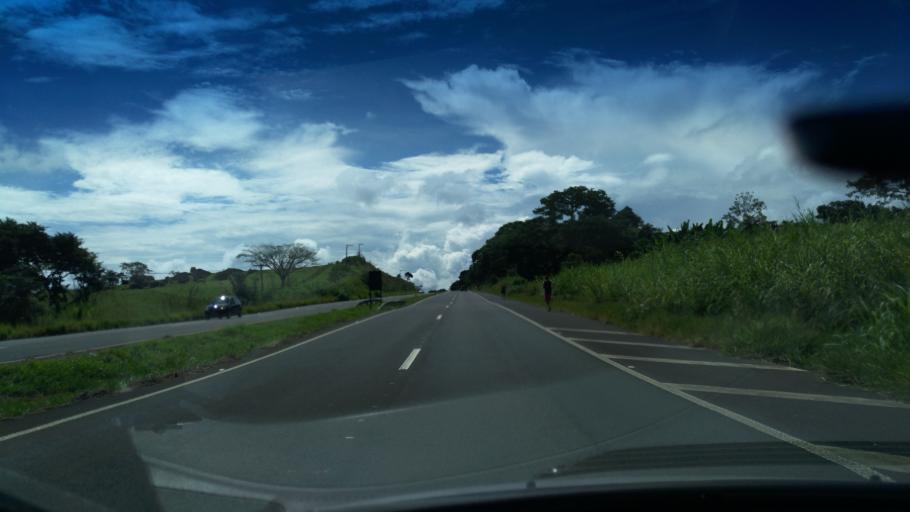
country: BR
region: Sao Paulo
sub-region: Santo Antonio Do Jardim
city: Espirito Santo do Pinhal
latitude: -22.1807
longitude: -46.7565
